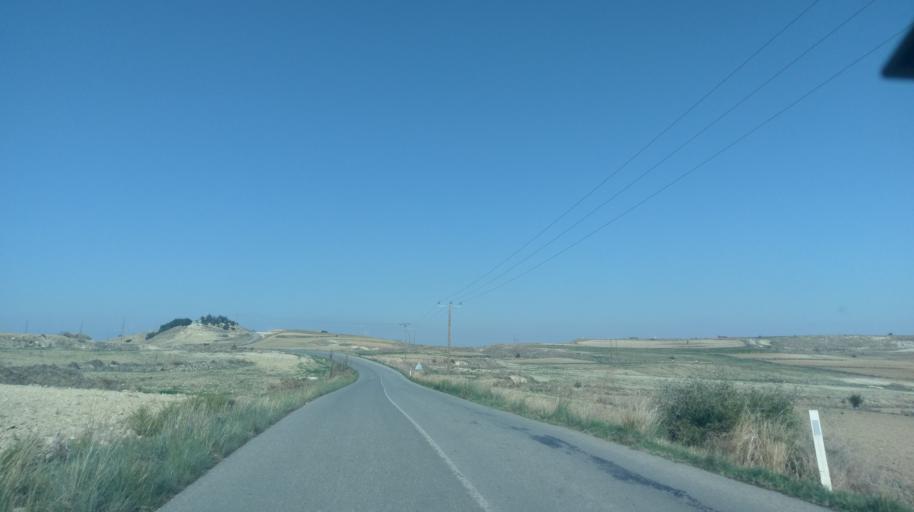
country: CY
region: Lefkosia
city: Lympia
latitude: 35.0441
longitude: 33.4824
